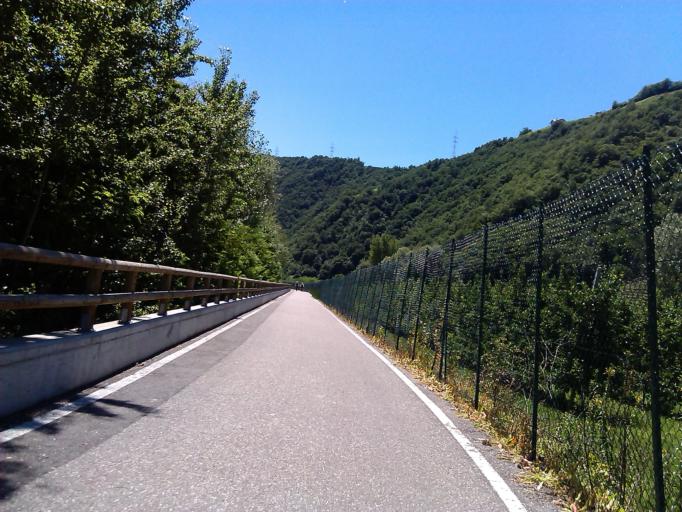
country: IT
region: Trentino-Alto Adige
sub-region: Bolzano
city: Cornaiano
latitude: 46.4633
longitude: 11.3028
